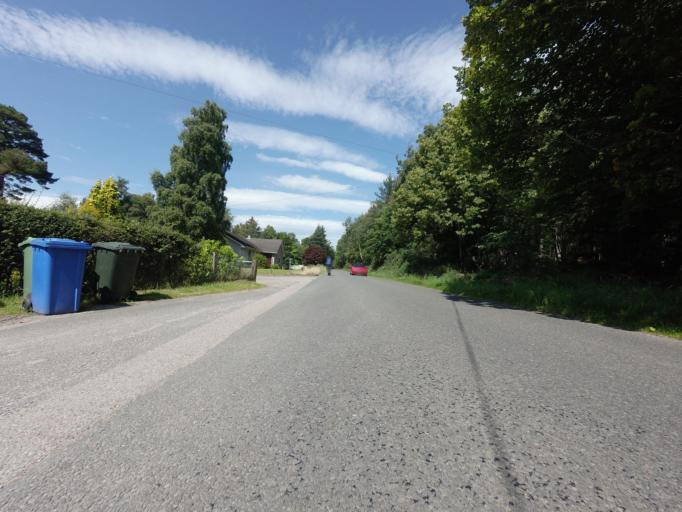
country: GB
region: Scotland
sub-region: Highland
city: Conon Bridge
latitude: 57.5364
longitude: -4.3253
